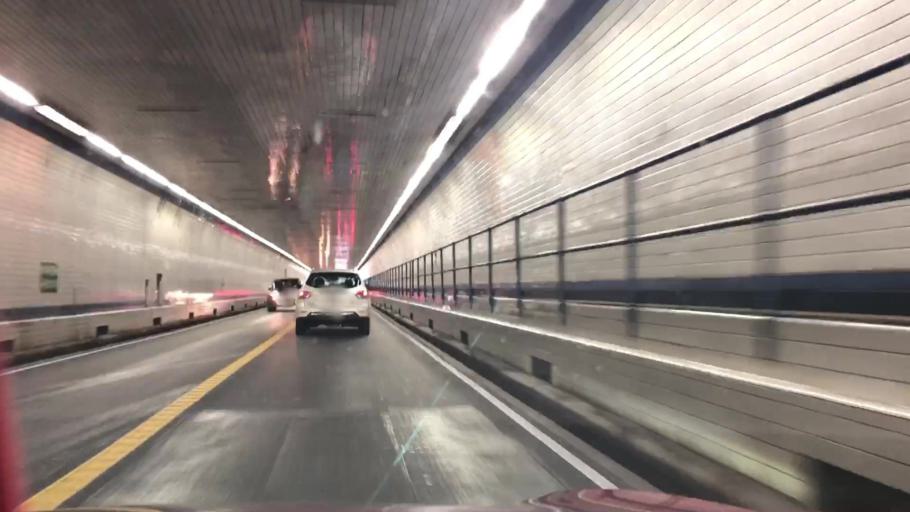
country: US
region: Virginia
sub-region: City of Virginia Beach
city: Virginia Beach
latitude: 37.0447
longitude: -76.0659
